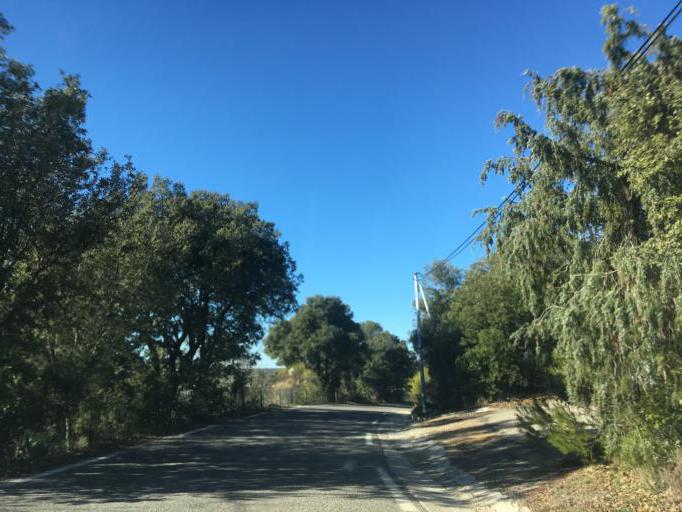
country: FR
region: Provence-Alpes-Cote d'Azur
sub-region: Departement du Var
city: Barjols
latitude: 43.5927
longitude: 6.0349
